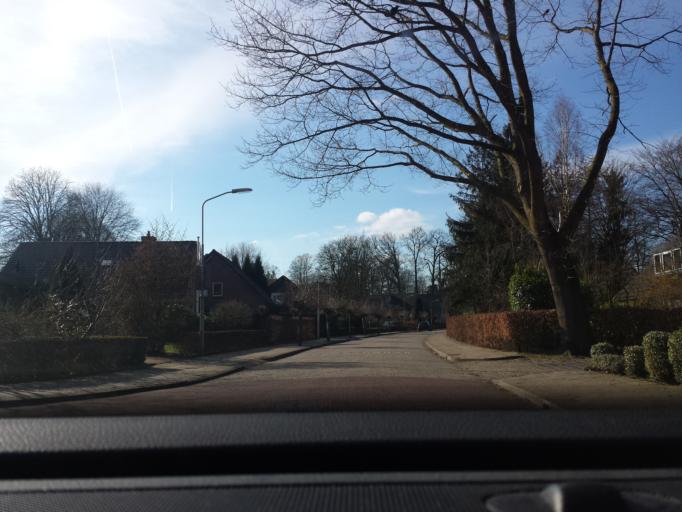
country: NL
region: Gelderland
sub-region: Gemeente Lochem
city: Almen
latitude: 52.1056
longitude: 6.3107
